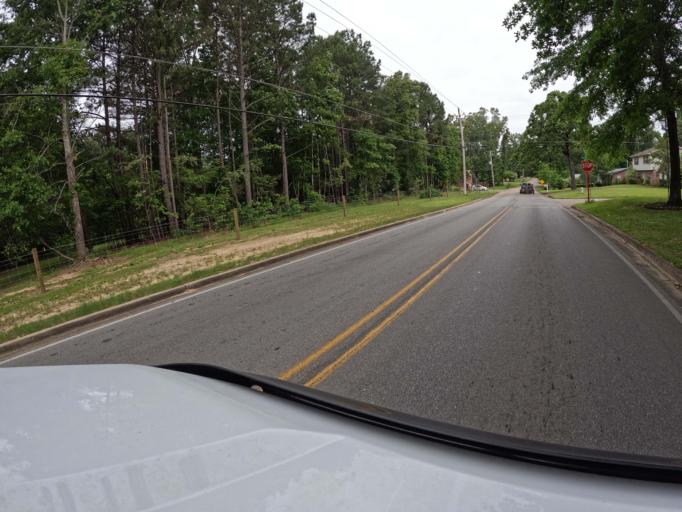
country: US
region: Mississippi
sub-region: Lee County
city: Tupelo
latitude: 34.2713
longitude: -88.7377
